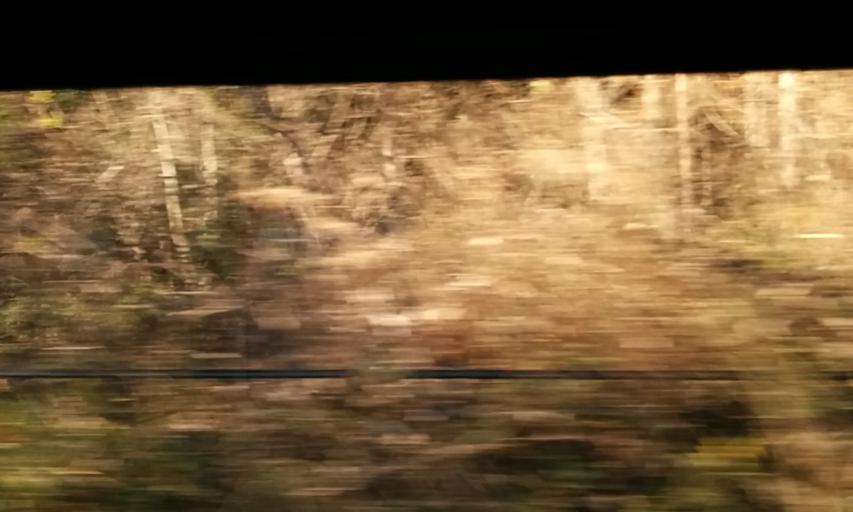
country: JP
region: Nagano
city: Iida
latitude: 35.6798
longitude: 137.6486
